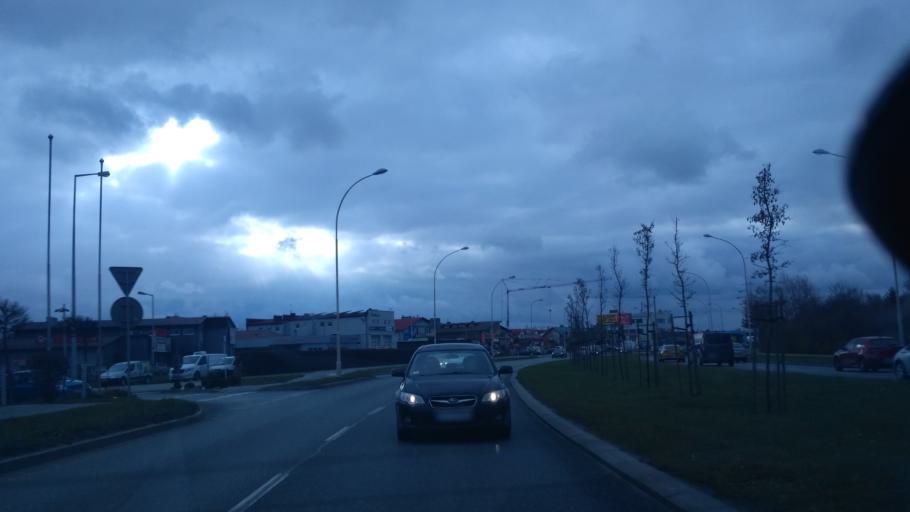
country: PL
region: Subcarpathian Voivodeship
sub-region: Rzeszow
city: Rzeszow
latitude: 50.0206
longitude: 22.0252
